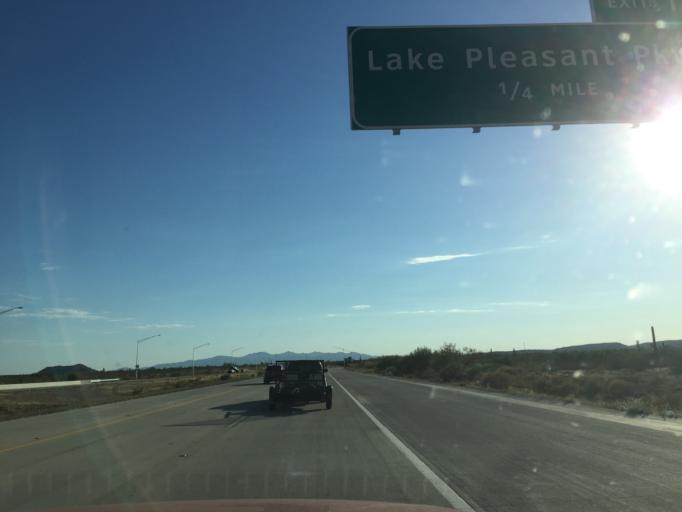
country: US
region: Arizona
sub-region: Maricopa County
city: Anthem
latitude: 33.7746
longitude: -112.2395
